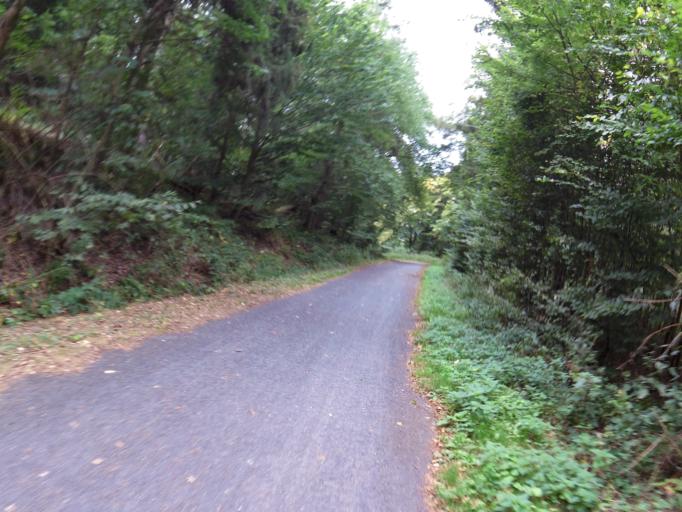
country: DE
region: North Rhine-Westphalia
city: Heimbach
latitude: 50.6221
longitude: 6.3953
